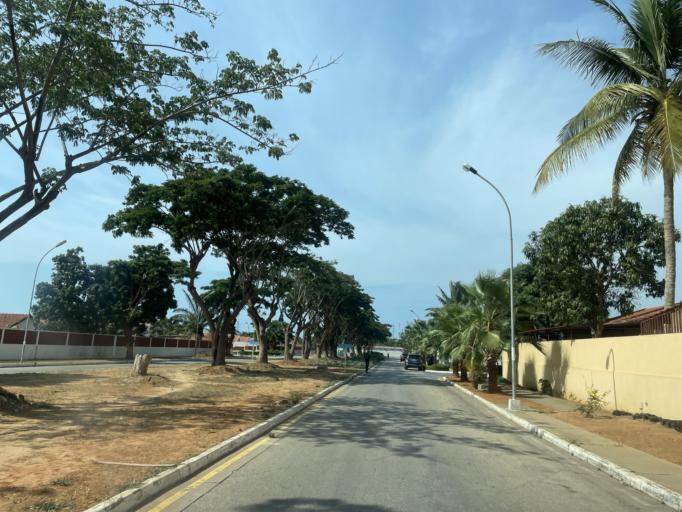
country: AO
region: Luanda
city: Luanda
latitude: -8.9119
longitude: 13.1807
